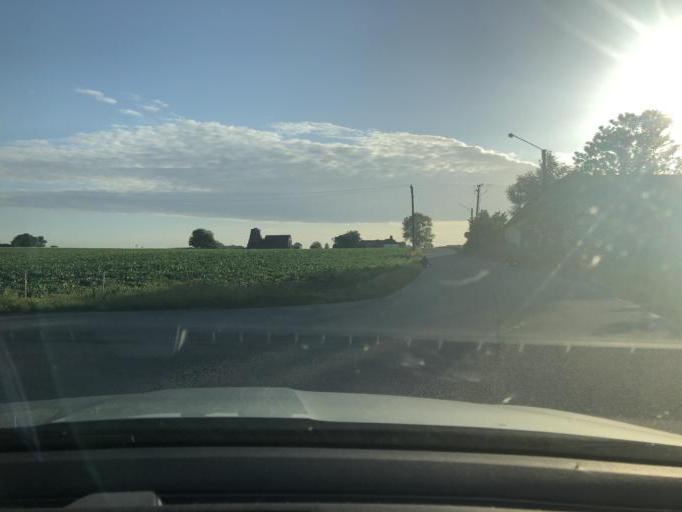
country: SE
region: Skane
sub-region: Simrishamns Kommun
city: Simrishamn
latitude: 55.4998
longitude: 14.2035
